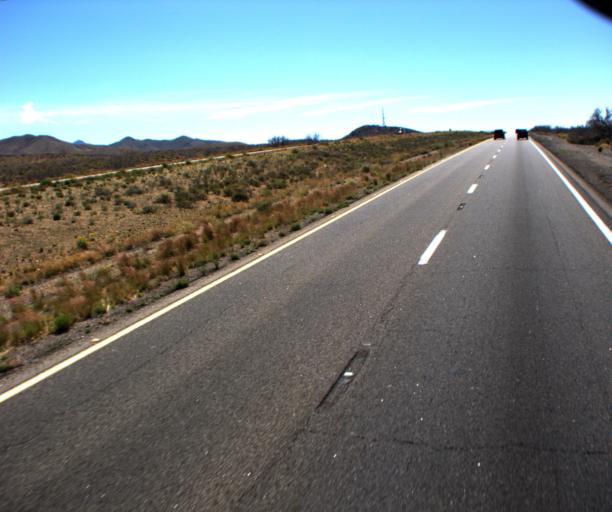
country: US
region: Arizona
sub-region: Mohave County
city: Dolan Springs
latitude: 35.4476
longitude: -114.2960
